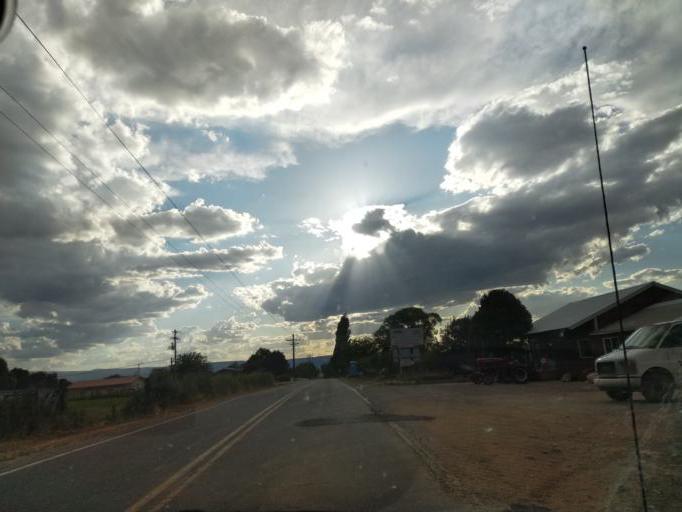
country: US
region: Colorado
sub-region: Mesa County
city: Clifton
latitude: 39.0559
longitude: -108.4206
